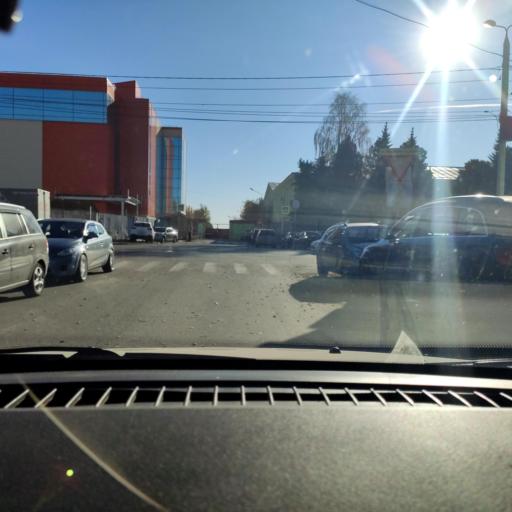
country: RU
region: Perm
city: Perm
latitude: 58.1106
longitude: 56.3718
